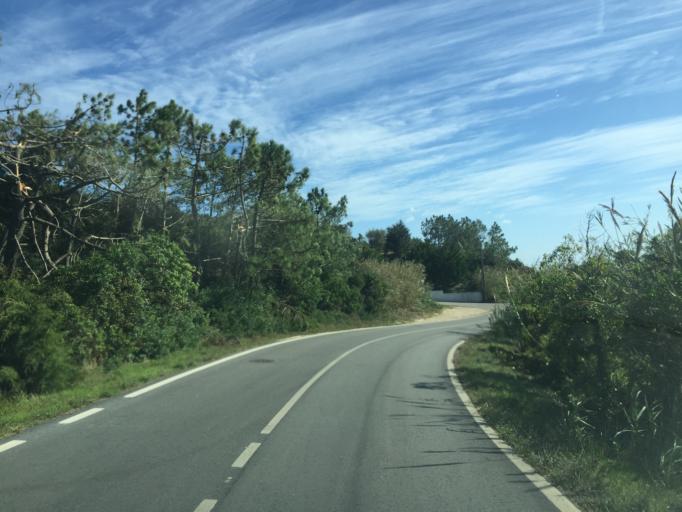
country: PT
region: Coimbra
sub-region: Figueira da Foz
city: Buarcos
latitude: 40.1803
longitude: -8.9051
